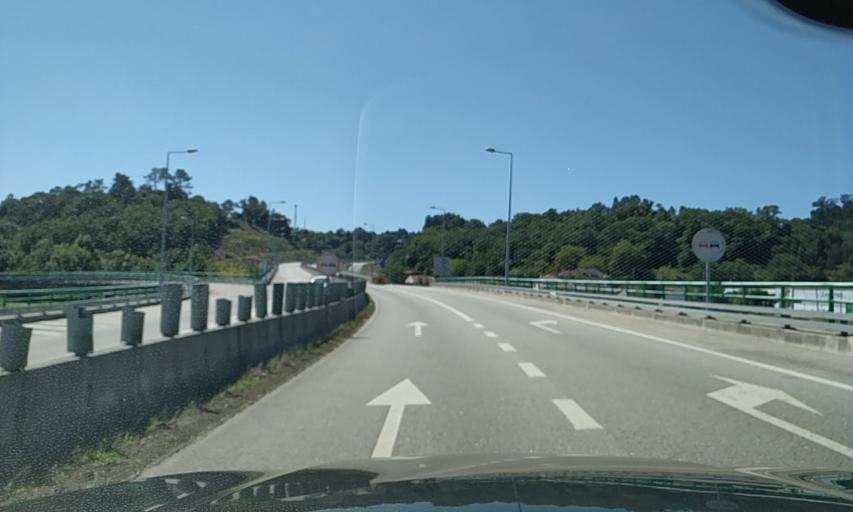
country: PT
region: Aveiro
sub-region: Agueda
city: Agueda
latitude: 40.5682
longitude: -8.4484
